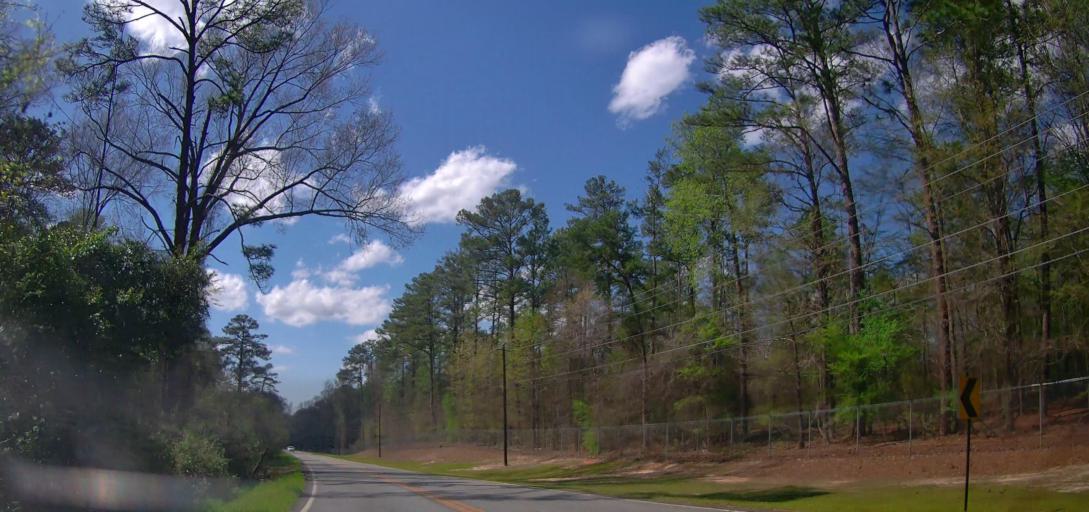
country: US
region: Georgia
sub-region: Bibb County
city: Macon
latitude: 32.8142
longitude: -83.5416
